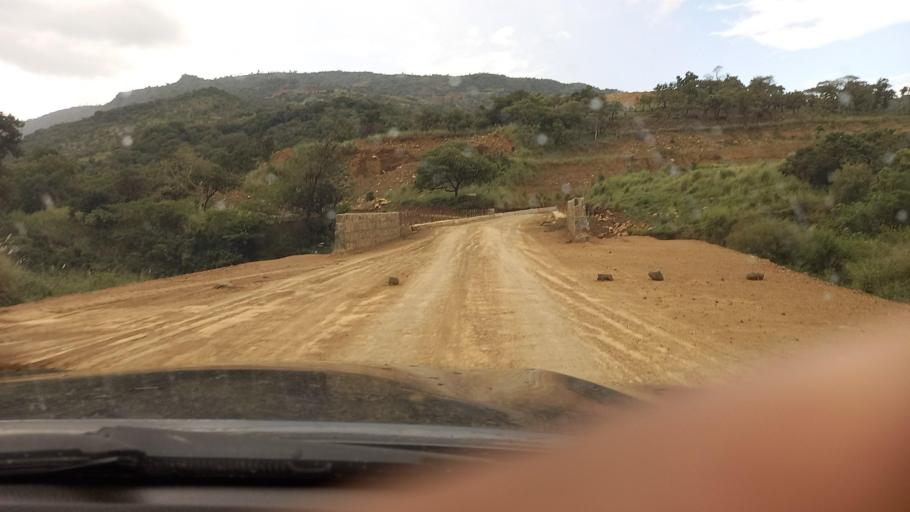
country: ET
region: Southern Nations, Nationalities, and People's Region
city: Mizan Teferi
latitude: 6.1888
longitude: 35.6744
